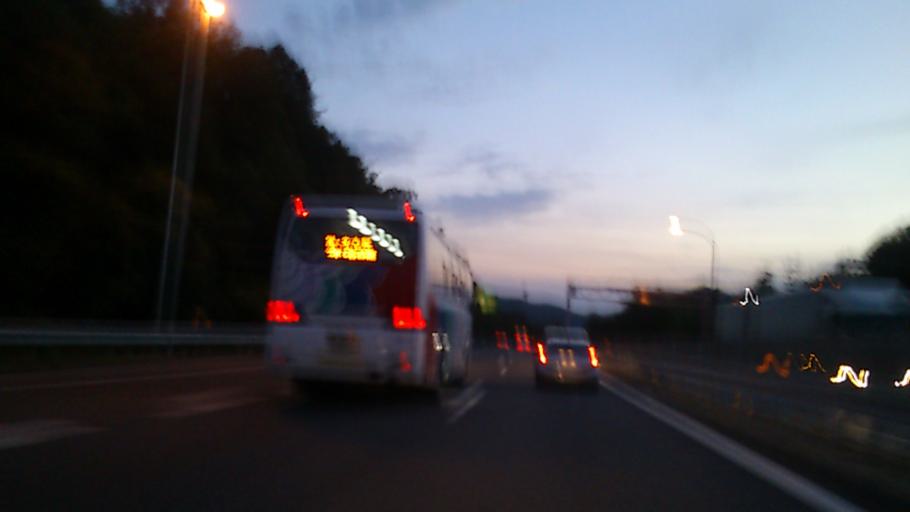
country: JP
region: Gifu
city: Tajimi
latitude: 35.3332
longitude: 137.0413
